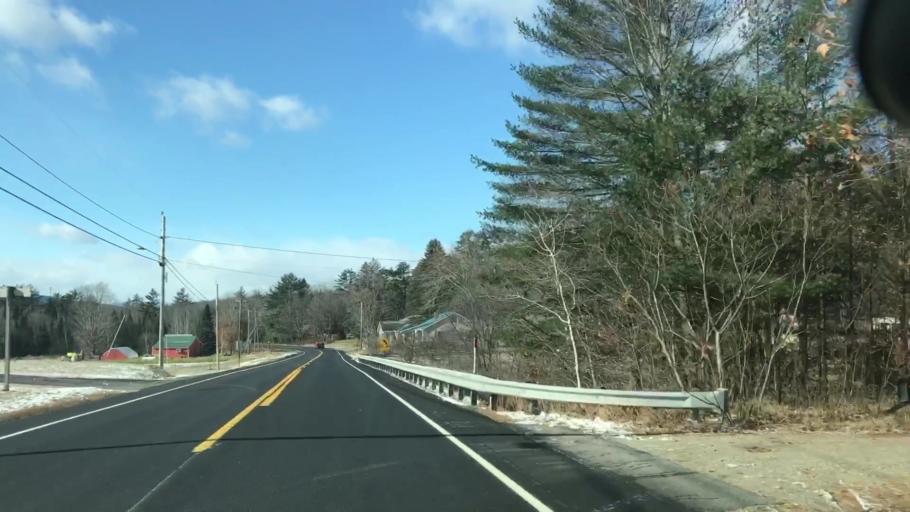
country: US
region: Maine
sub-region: Oxford County
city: Porter
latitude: 43.7955
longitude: -70.9394
